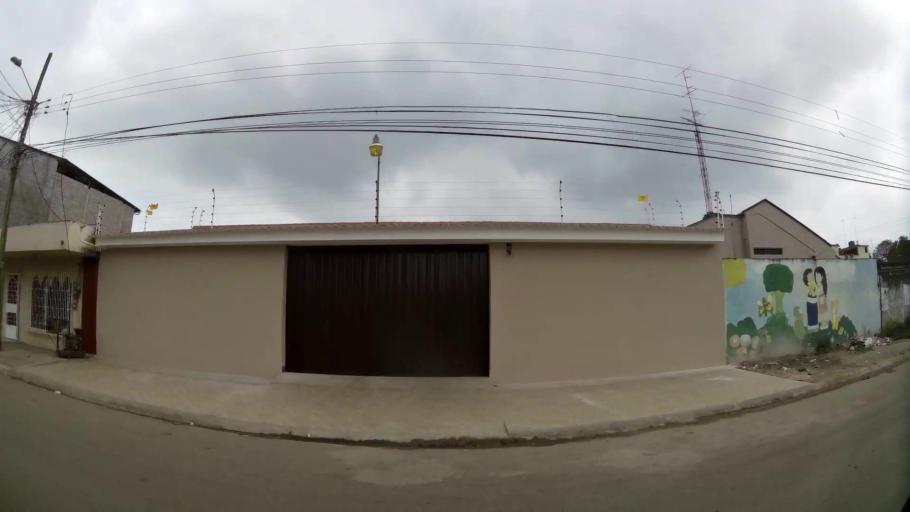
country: EC
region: El Oro
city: Pasaje
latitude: -3.2444
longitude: -79.8349
